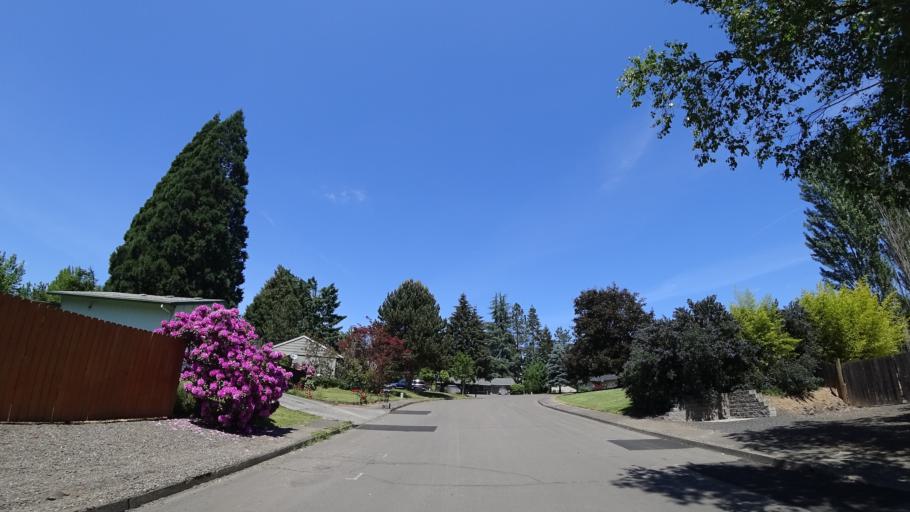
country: US
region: Oregon
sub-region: Washington County
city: Tigard
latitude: 45.4366
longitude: -122.7993
